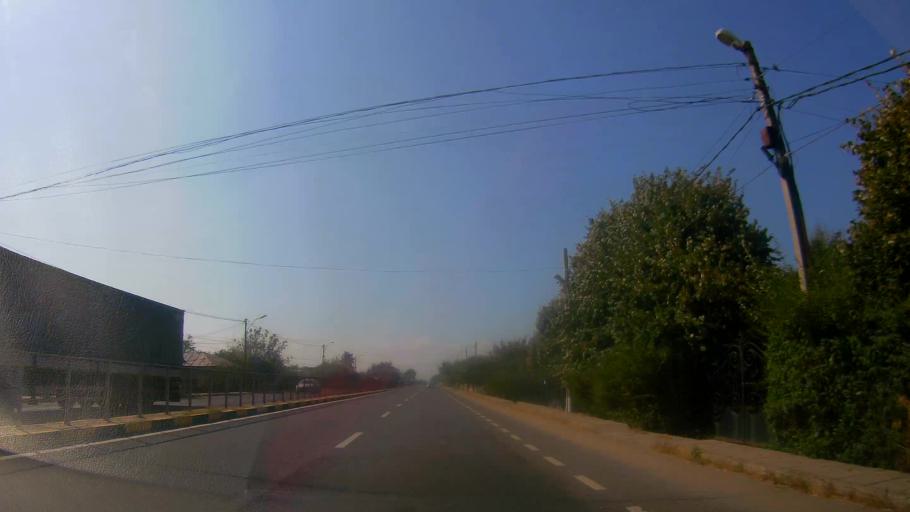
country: RO
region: Giurgiu
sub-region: Comuna Fratesti
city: Remus
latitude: 43.9483
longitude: 25.9802
